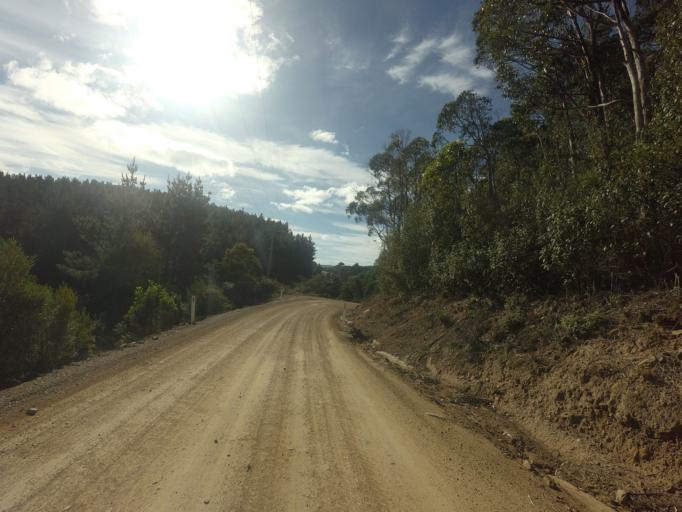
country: AU
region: Tasmania
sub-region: Clarence
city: Sandford
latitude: -43.1802
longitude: 147.7708
